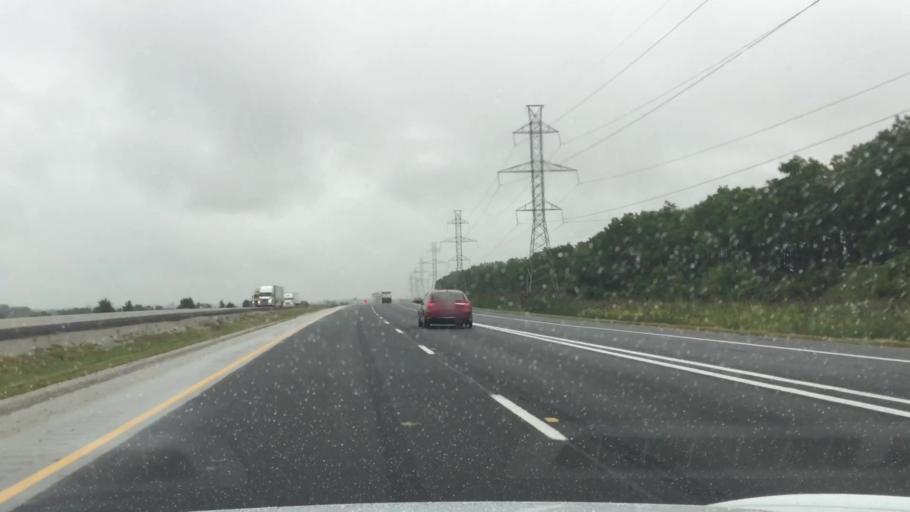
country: CA
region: Ontario
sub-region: Lambton County
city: Walpole Island
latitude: 42.3526
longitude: -82.1805
